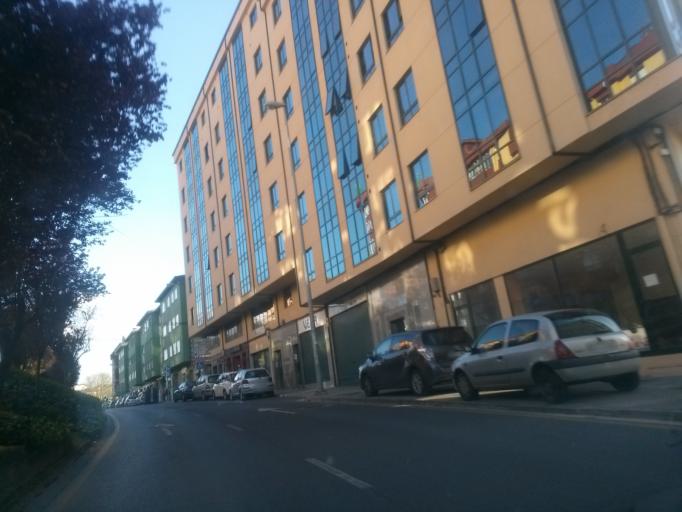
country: ES
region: Galicia
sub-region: Provincia de Lugo
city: Lugo
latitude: 43.0056
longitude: -7.5642
